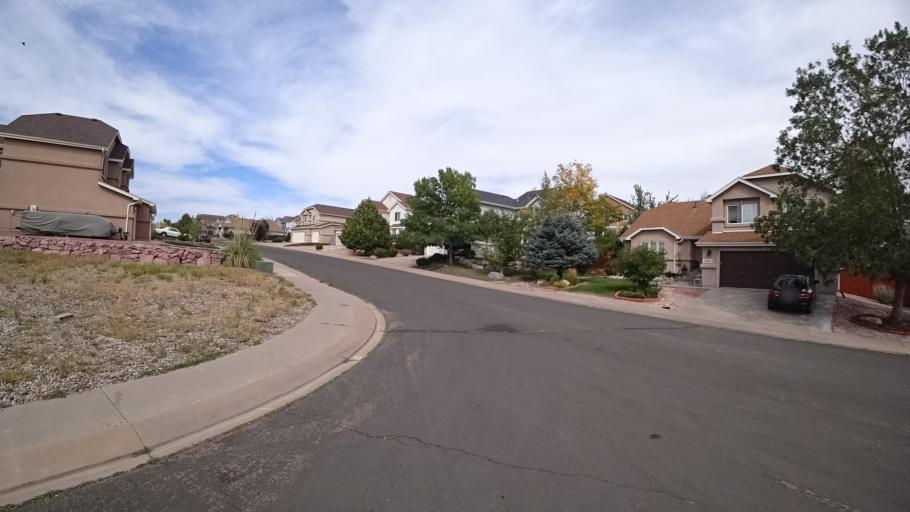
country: US
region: Colorado
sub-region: El Paso County
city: Cimarron Hills
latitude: 38.9082
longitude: -104.7009
